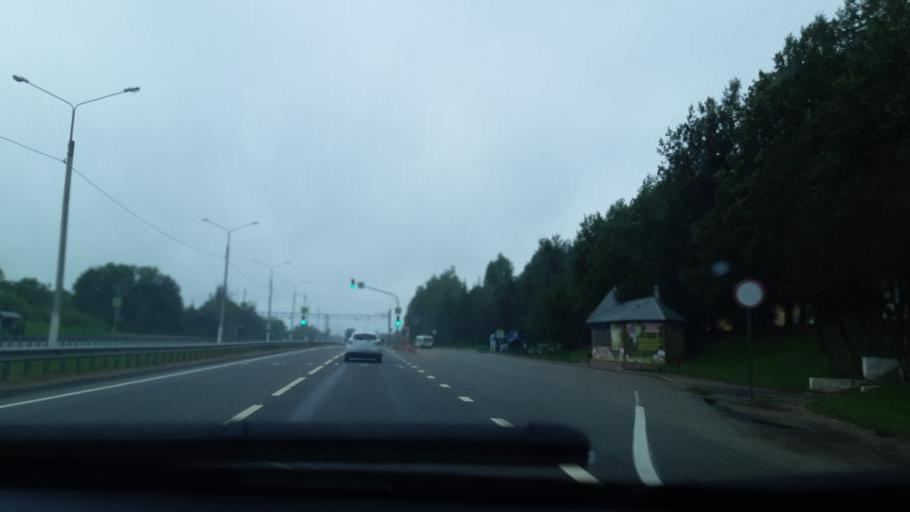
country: RU
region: Smolensk
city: Talashkino
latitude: 54.6804
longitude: 32.1411
